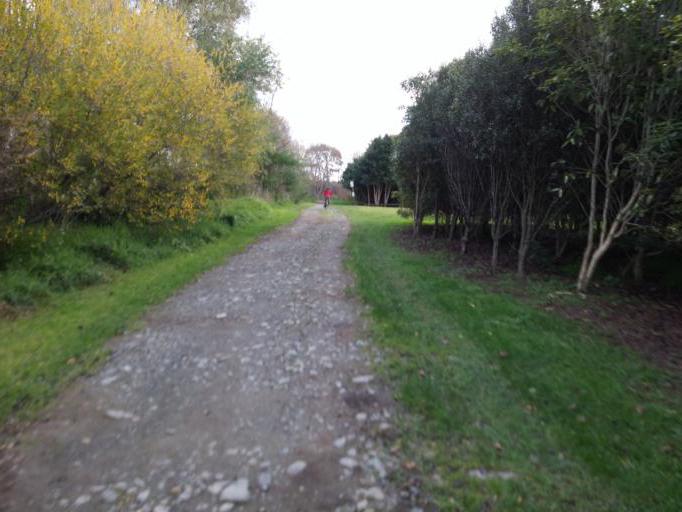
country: NZ
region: Wellington
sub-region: Kapiti Coast District
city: Paraparaumu
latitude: -40.8816
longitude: 175.0430
